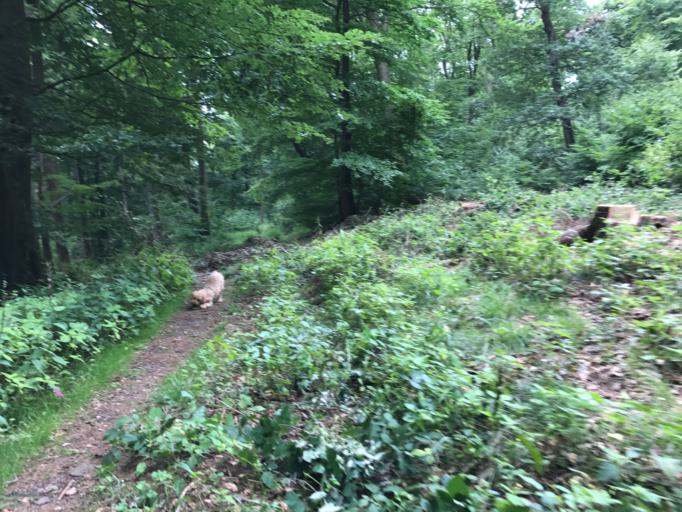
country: DE
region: Hesse
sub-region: Regierungsbezirk Darmstadt
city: Schlangenbad
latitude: 50.1023
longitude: 8.1338
